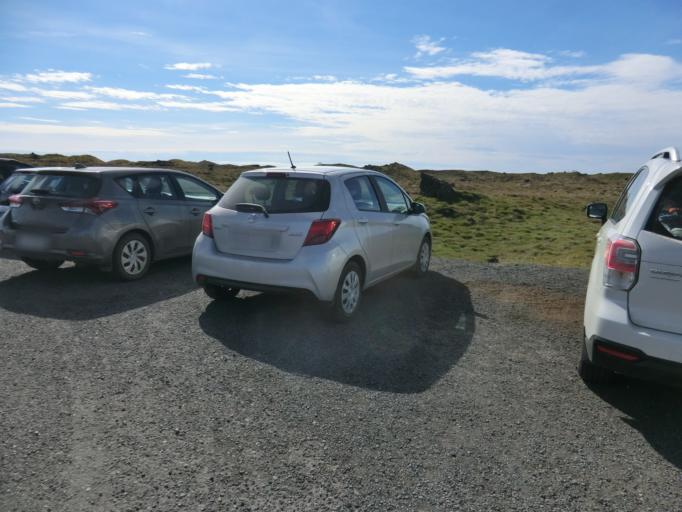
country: IS
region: West
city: Olafsvik
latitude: 64.7535
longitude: -23.8954
